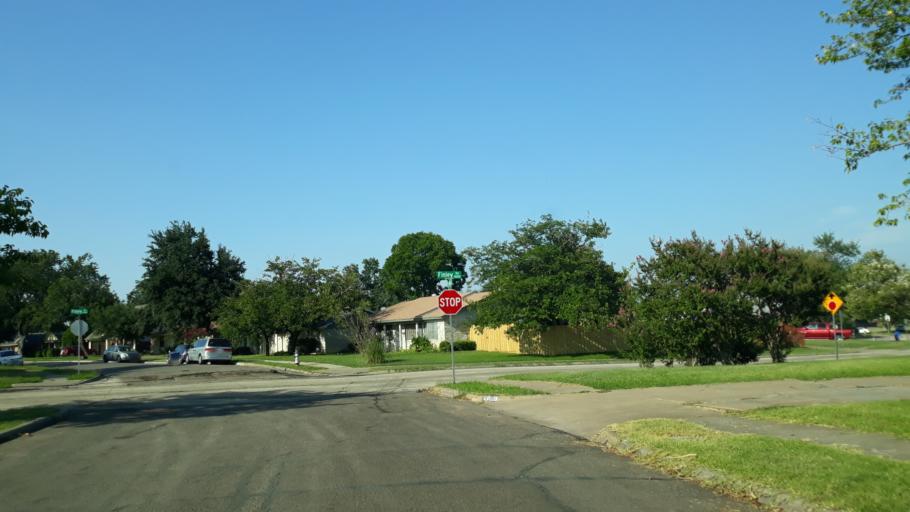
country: US
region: Texas
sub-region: Dallas County
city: Irving
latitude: 32.8509
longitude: -97.0056
